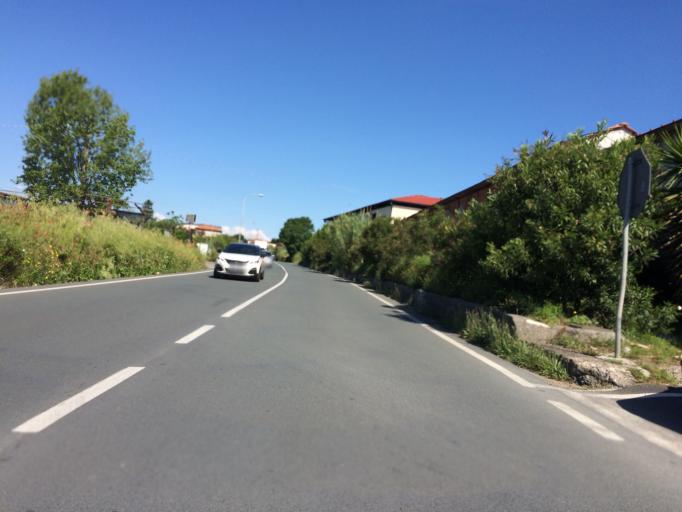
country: IT
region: Liguria
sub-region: Provincia di La Spezia
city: Colombiera-Molicciara
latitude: 44.0889
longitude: 10.0010
